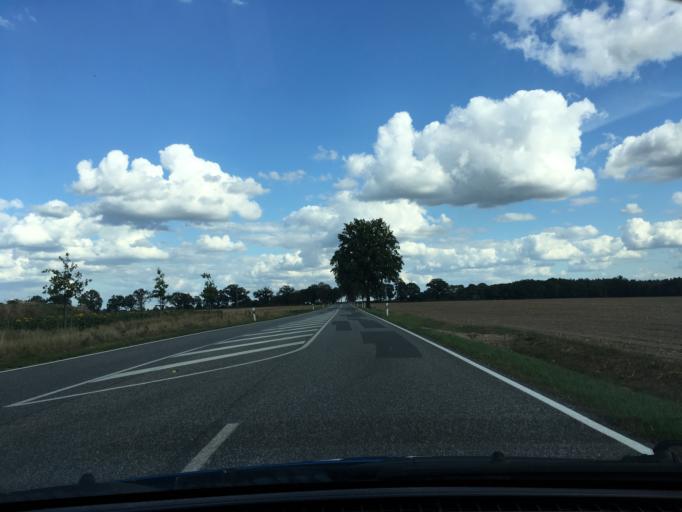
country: DE
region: Mecklenburg-Vorpommern
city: Lubtheen
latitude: 53.3763
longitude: 11.0867
